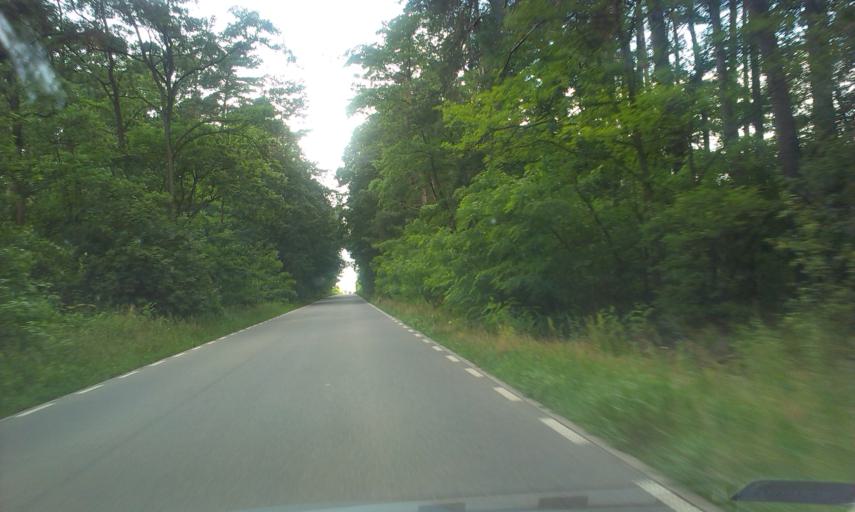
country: PL
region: Masovian Voivodeship
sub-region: Powiat zyrardowski
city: Radziejowice
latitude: 51.9686
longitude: 20.5860
